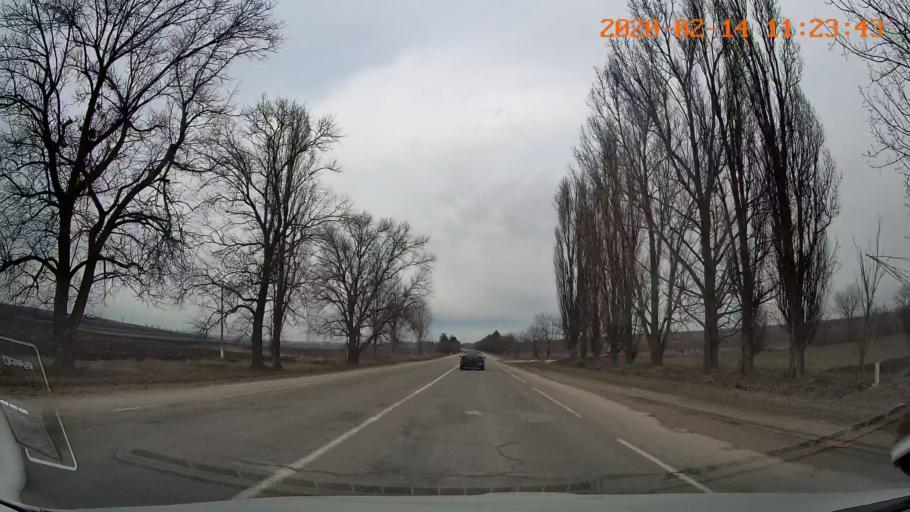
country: MD
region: Briceni
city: Briceni
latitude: 48.3282
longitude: 27.1227
